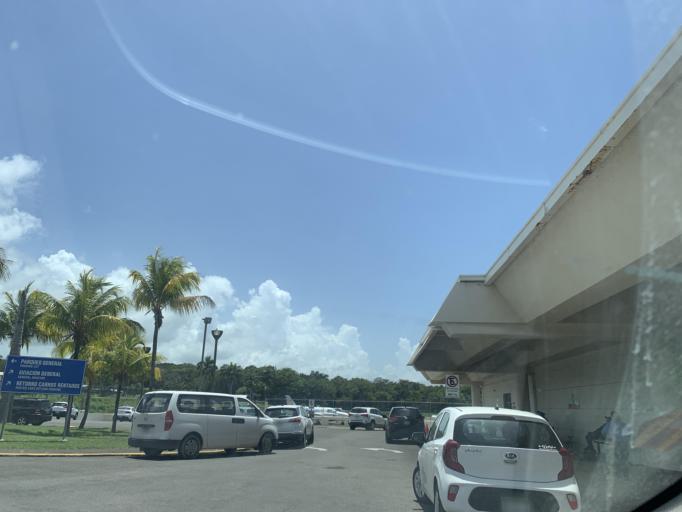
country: DO
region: Puerto Plata
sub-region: Puerto Plata
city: Puerto Plata
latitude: 19.7547
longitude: -70.5634
